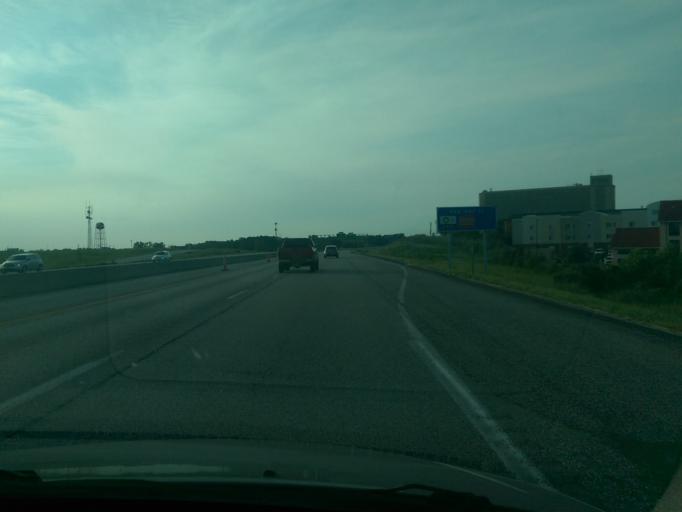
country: US
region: Missouri
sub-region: Platte County
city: Weatherby Lake
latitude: 39.2913
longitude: -94.6823
